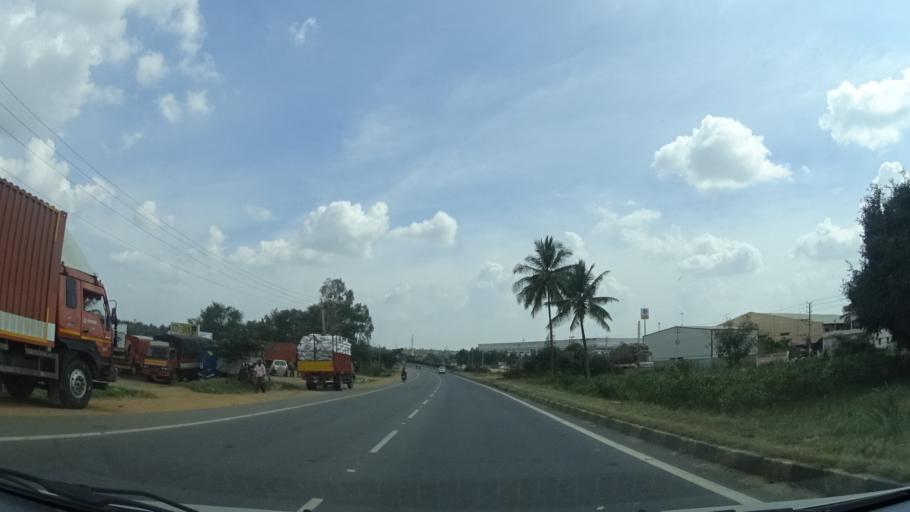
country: IN
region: Karnataka
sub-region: Bangalore Rural
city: Nelamangala
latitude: 13.1468
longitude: 77.3416
